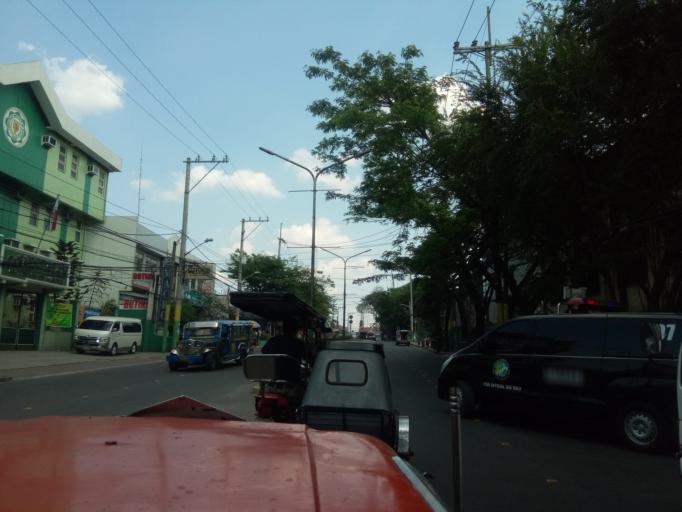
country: PH
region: Calabarzon
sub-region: Province of Cavite
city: Dasmarinas
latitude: 14.3252
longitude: 120.9618
